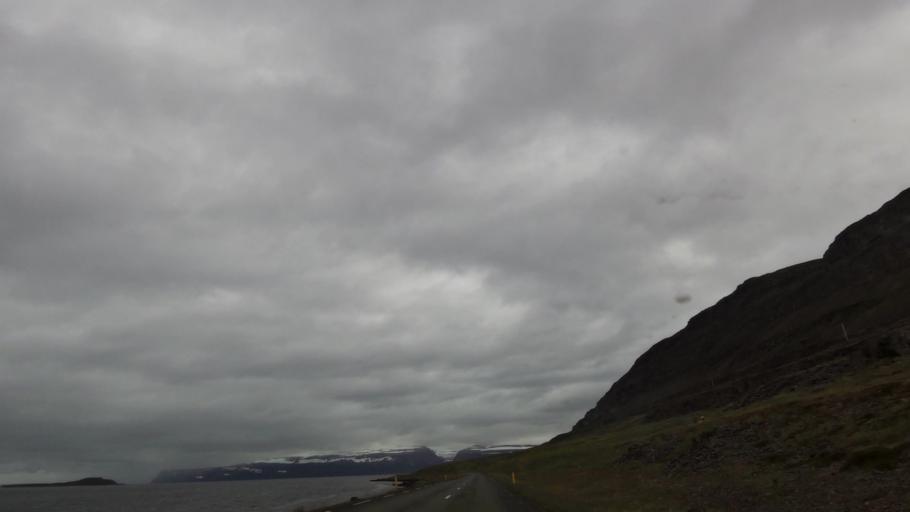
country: IS
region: Westfjords
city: Isafjoerdur
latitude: 66.0176
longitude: -22.7808
